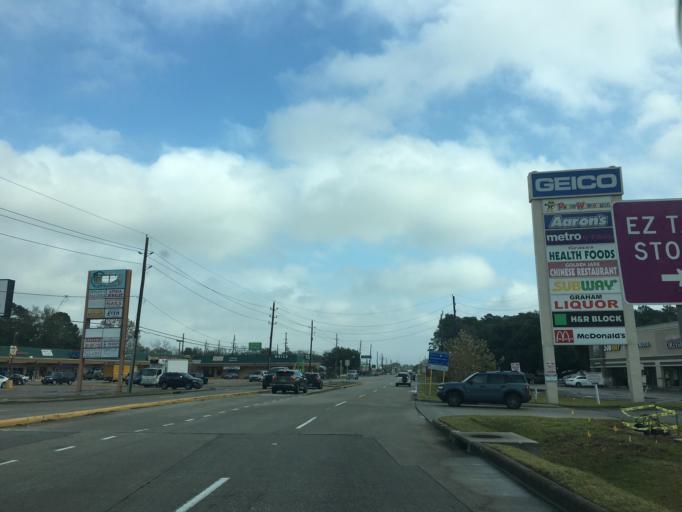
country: US
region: Texas
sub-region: Harris County
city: Spring
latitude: 30.0753
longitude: -95.4347
